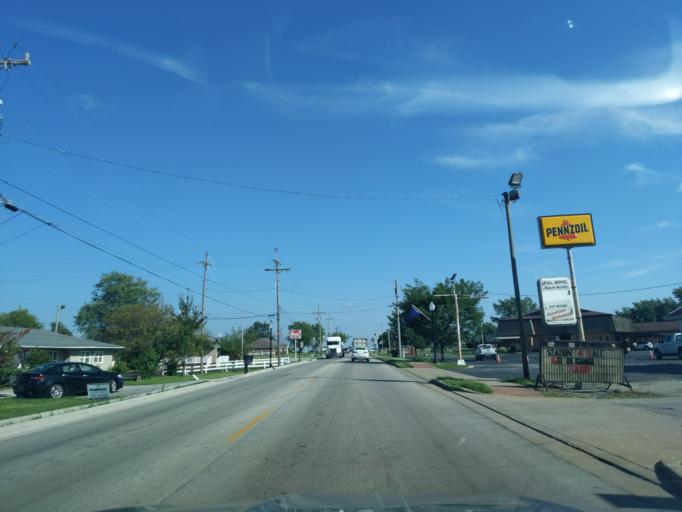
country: US
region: Indiana
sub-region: Ripley County
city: Osgood
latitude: 39.1244
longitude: -85.2885
